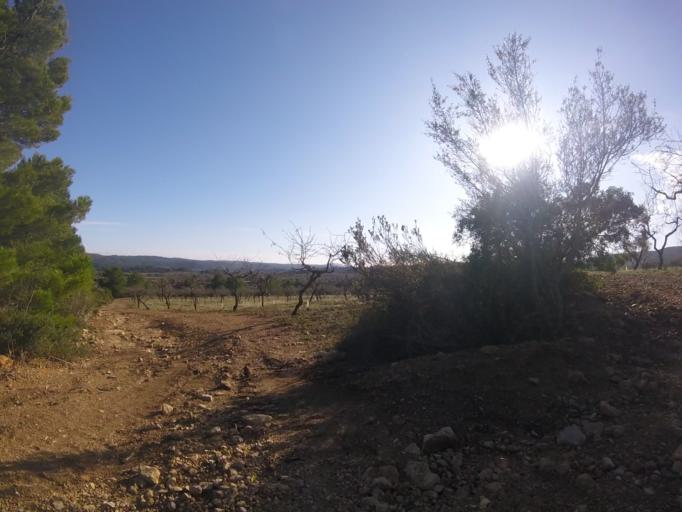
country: ES
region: Valencia
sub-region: Provincia de Castello
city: Sarratella
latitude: 40.2839
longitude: 0.0653
